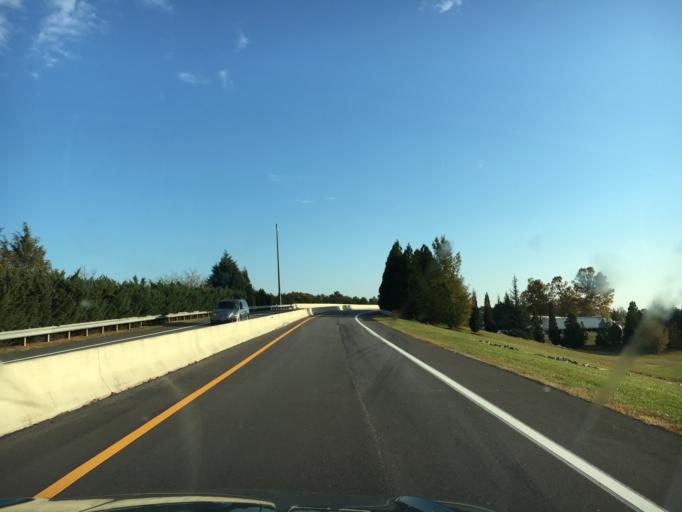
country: US
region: South Carolina
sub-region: Greenville County
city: Greer
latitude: 34.8787
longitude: -82.2139
